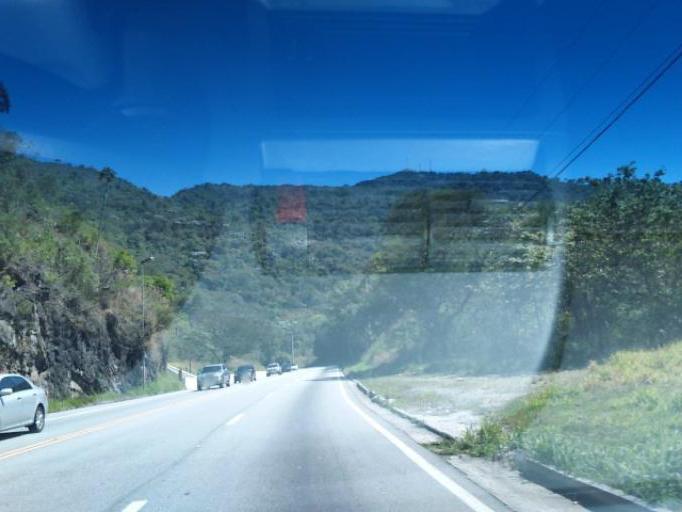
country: BR
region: Sao Paulo
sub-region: Campos Do Jordao
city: Campos do Jordao
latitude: -22.8449
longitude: -45.6190
